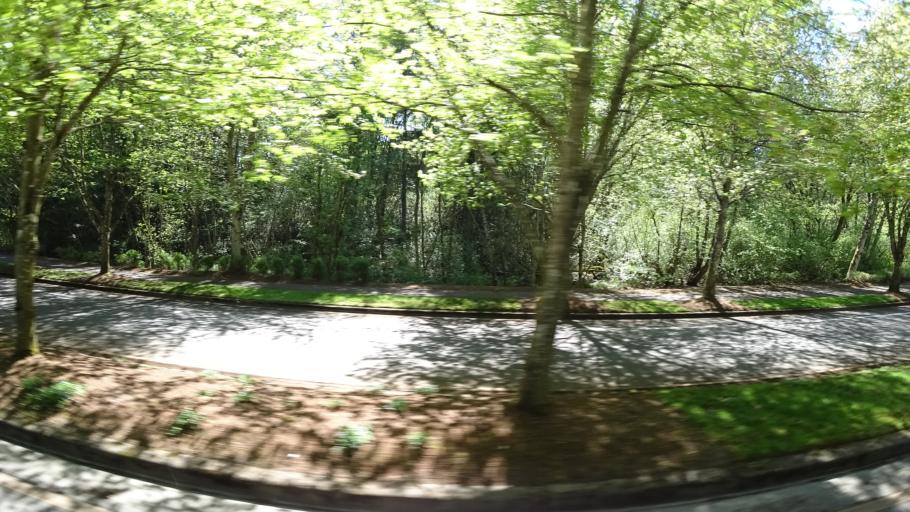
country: US
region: Oregon
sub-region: Washington County
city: King City
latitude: 45.4414
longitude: -122.8297
